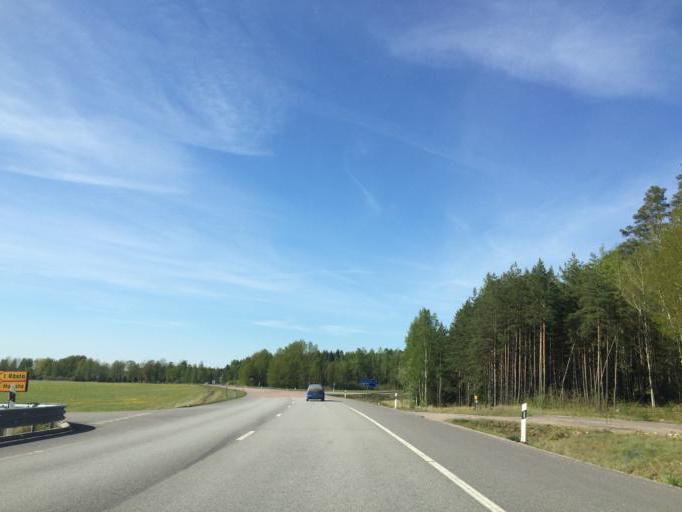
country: SE
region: Vaestmanland
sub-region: Kungsors Kommun
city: Kungsoer
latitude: 59.3997
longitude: 16.1078
